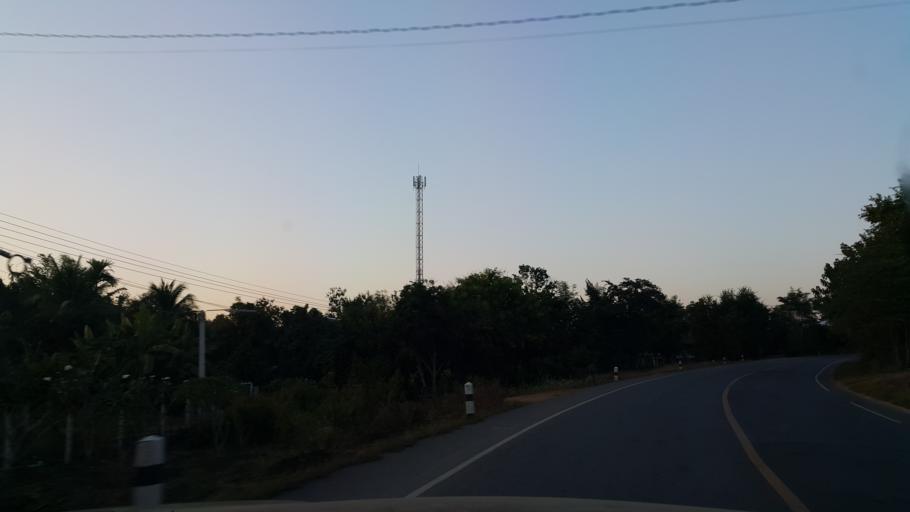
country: TH
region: Phrae
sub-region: Amphoe Wang Chin
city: Wang Chin
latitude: 17.8473
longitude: 99.6283
